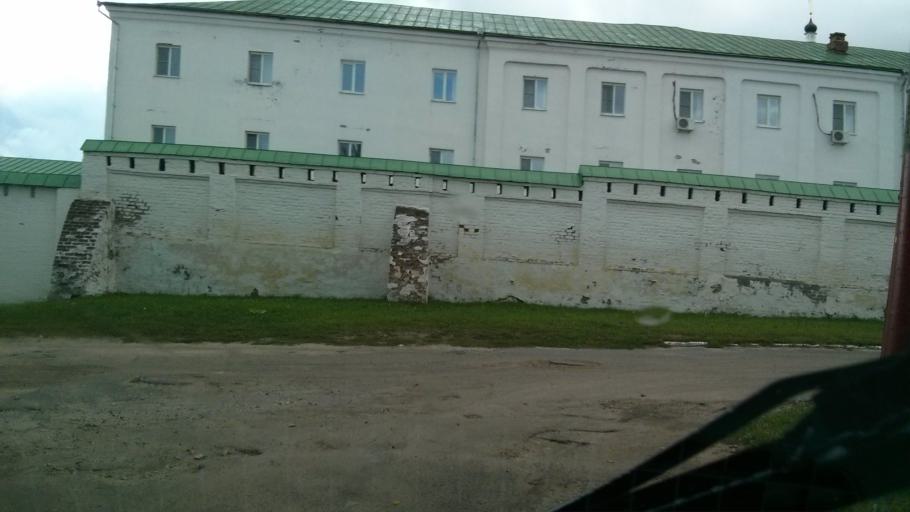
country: RU
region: Vladimir
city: Murom
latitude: 55.5740
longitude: 42.0661
